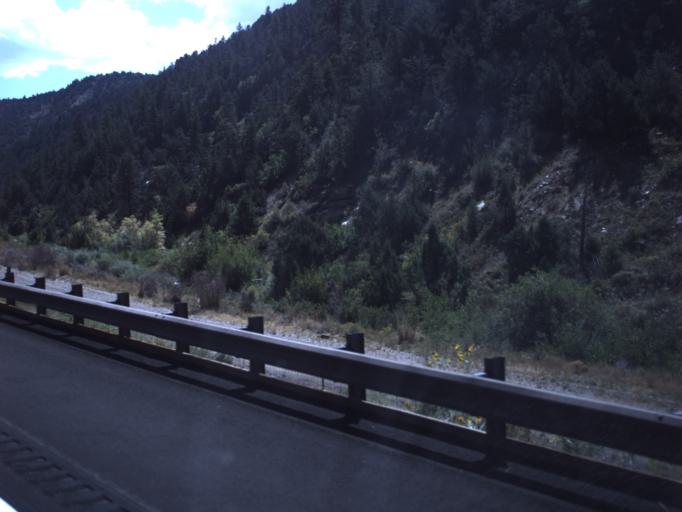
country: US
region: Utah
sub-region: Sevier County
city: Salina
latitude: 38.8921
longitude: -111.6173
